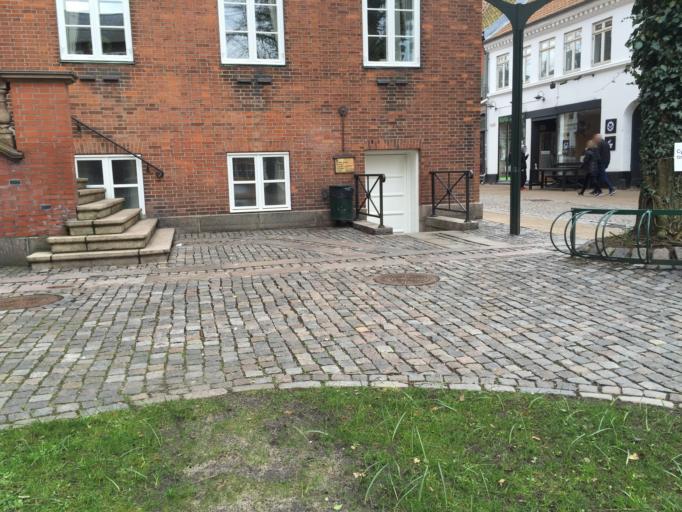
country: DK
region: South Denmark
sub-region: Kolding Kommune
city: Kolding
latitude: 55.4903
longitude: 9.4728
